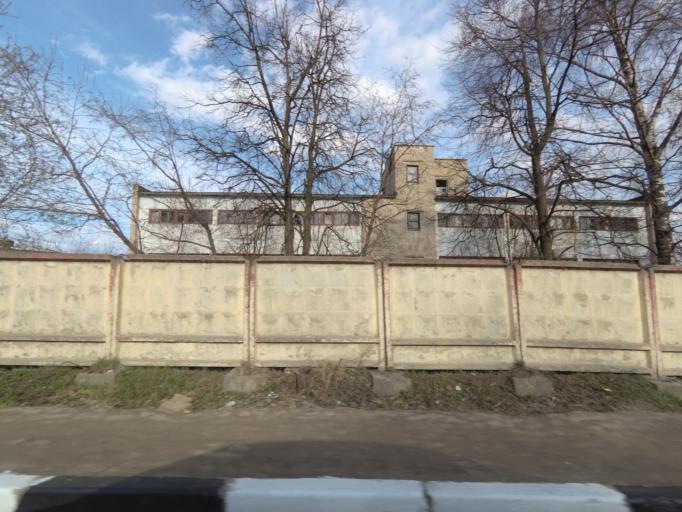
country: RU
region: Moskovskaya
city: Lobnya
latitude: 56.0139
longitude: 37.4374
